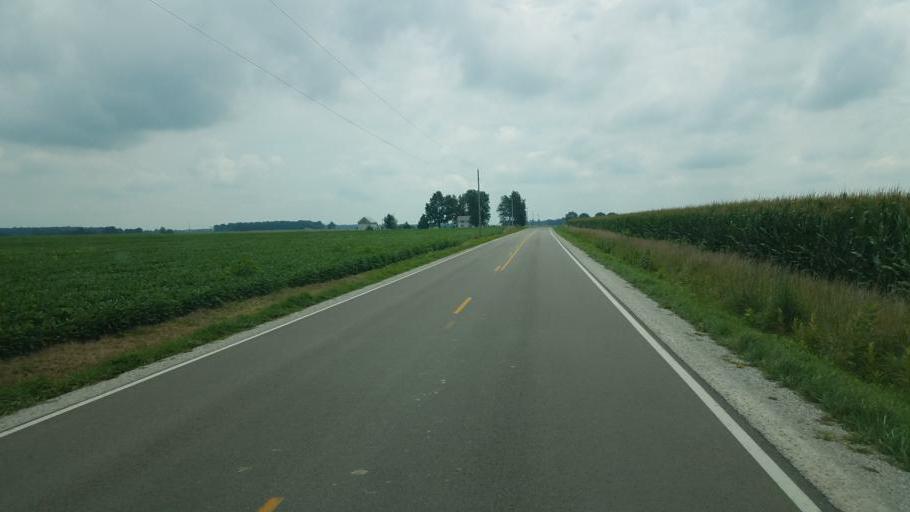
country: US
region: Ohio
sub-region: Crawford County
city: Bucyrus
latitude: 40.7180
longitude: -82.9724
